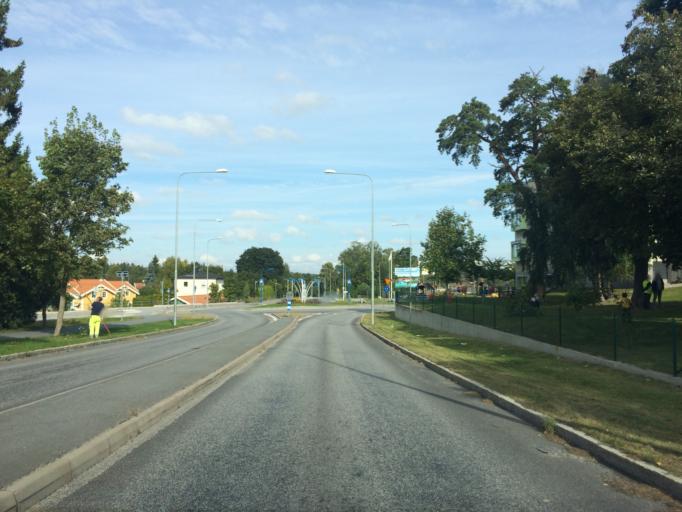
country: SE
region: Stockholm
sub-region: Sollentuna Kommun
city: Sollentuna
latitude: 59.4338
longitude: 17.9496
